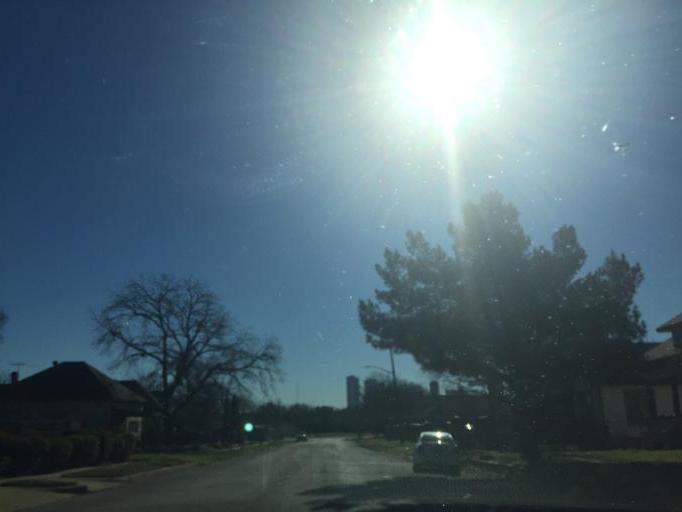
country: US
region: Texas
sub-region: Tarrant County
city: River Oaks
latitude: 32.7747
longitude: -97.3472
